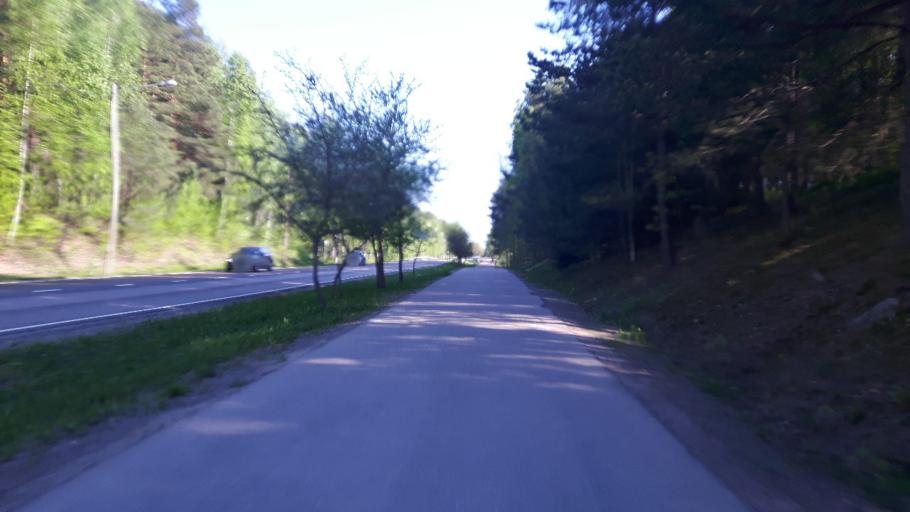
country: FI
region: Kymenlaakso
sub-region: Kotka-Hamina
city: Kotka
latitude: 60.4641
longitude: 26.8816
